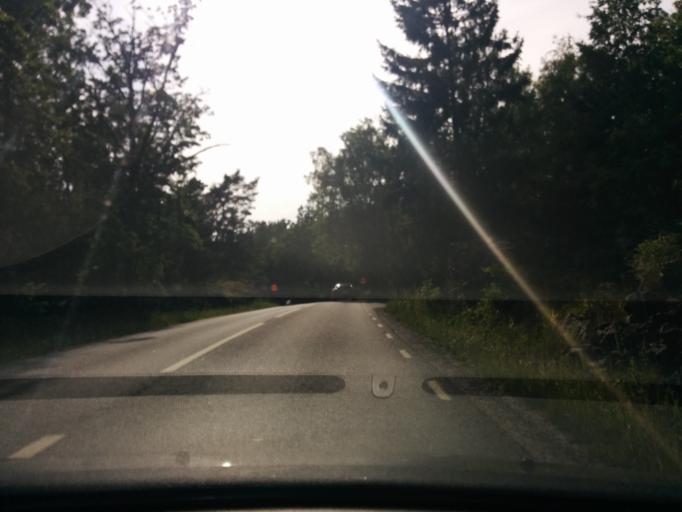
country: SE
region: Stockholm
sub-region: Varmdo Kommun
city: Holo
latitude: 59.2879
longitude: 18.6590
